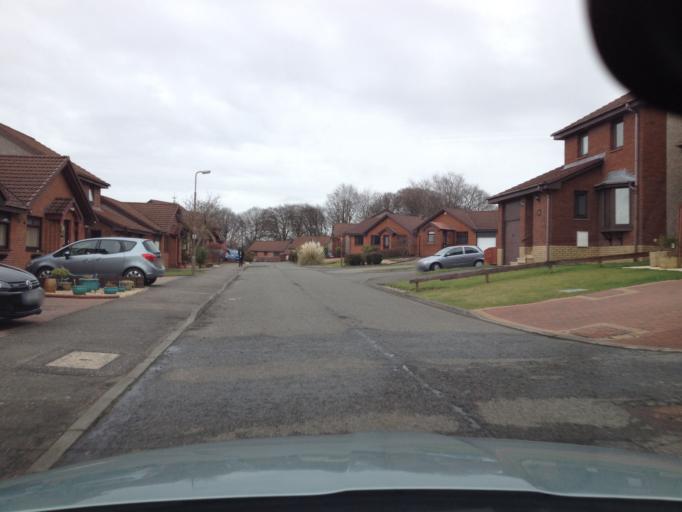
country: GB
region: Scotland
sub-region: West Lothian
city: Mid Calder
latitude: 55.8877
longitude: -3.4908
